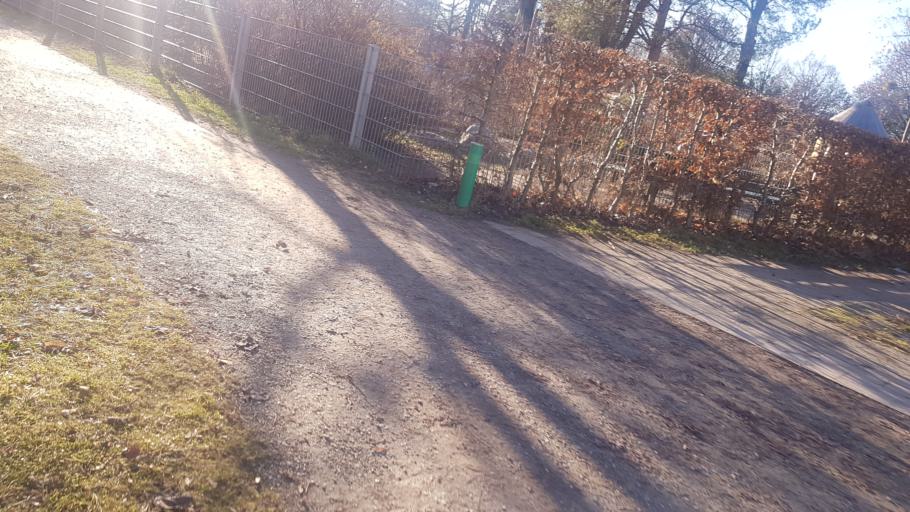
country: DE
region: Bavaria
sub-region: Upper Bavaria
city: Pasing
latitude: 48.1480
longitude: 11.5006
